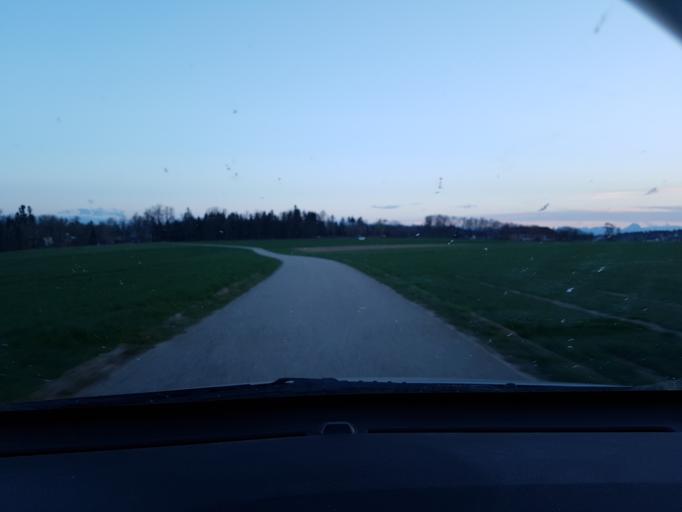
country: AT
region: Upper Austria
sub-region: Politischer Bezirk Linz-Land
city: Ansfelden
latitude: 48.1694
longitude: 14.3207
